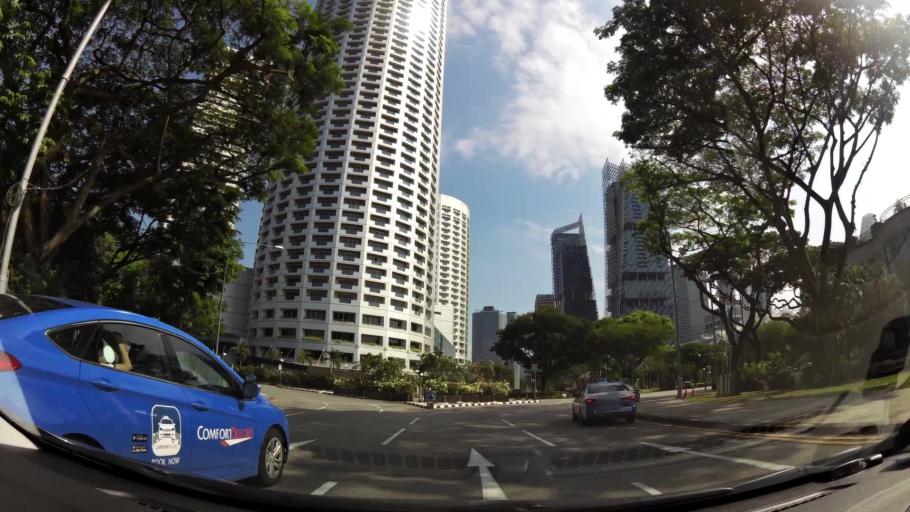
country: SG
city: Singapore
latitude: 1.2923
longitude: 103.8532
